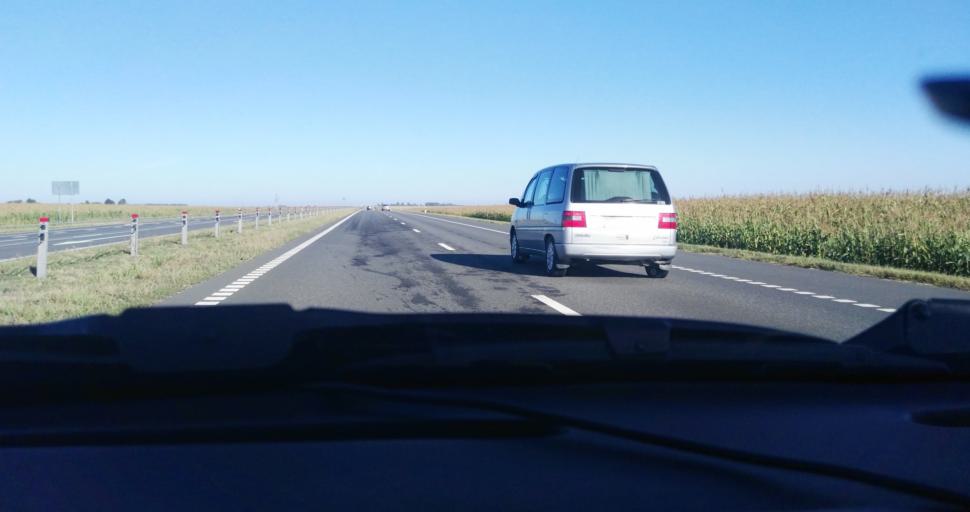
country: BY
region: Gomel
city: Buda-Kashalyova
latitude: 52.5245
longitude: 30.6189
